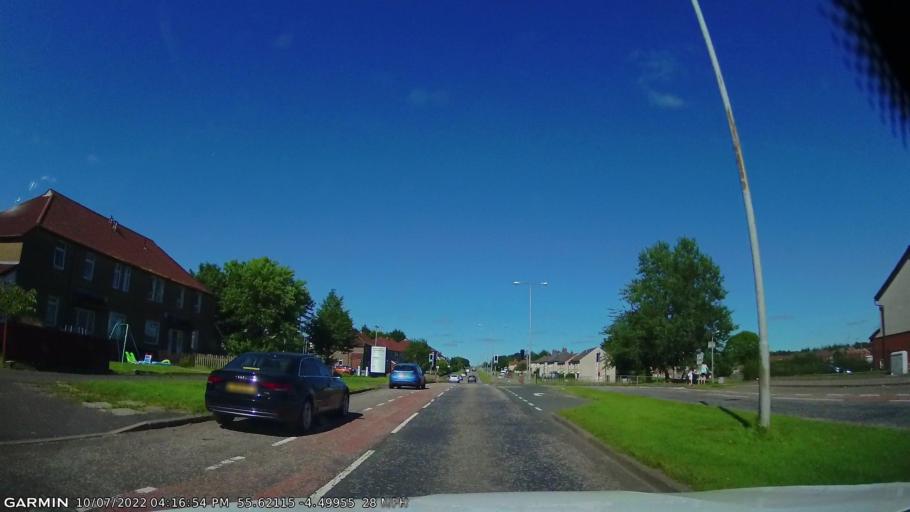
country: GB
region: Scotland
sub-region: East Ayrshire
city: Kilmarnock
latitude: 55.6212
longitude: -4.4995
